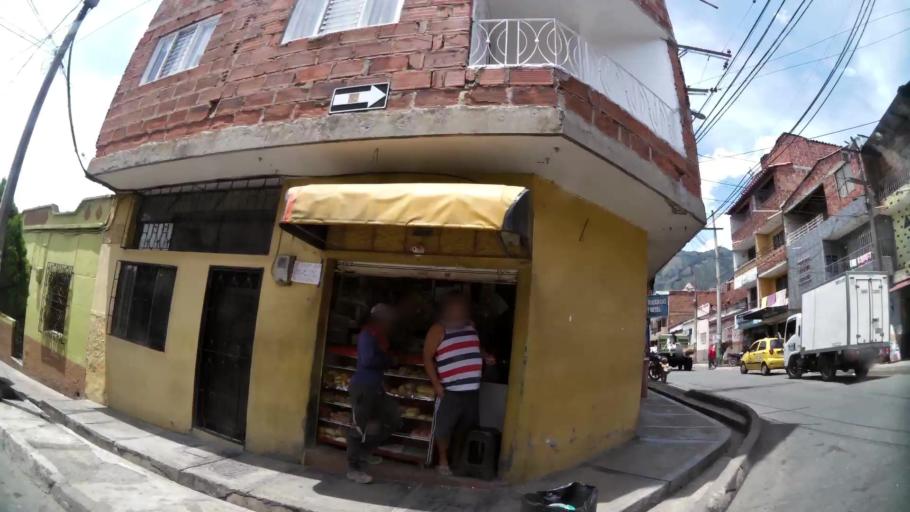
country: CO
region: Antioquia
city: Bello
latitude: 6.3496
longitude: -75.5670
